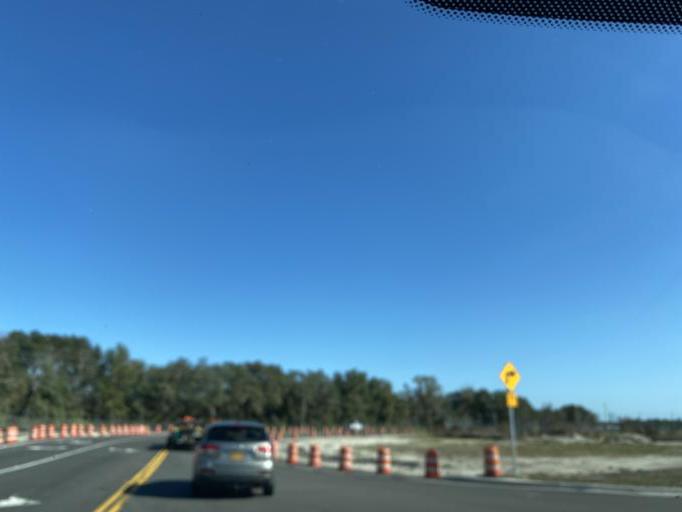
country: US
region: Florida
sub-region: Lake County
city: Mount Plymouth
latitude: 28.8121
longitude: -81.5110
